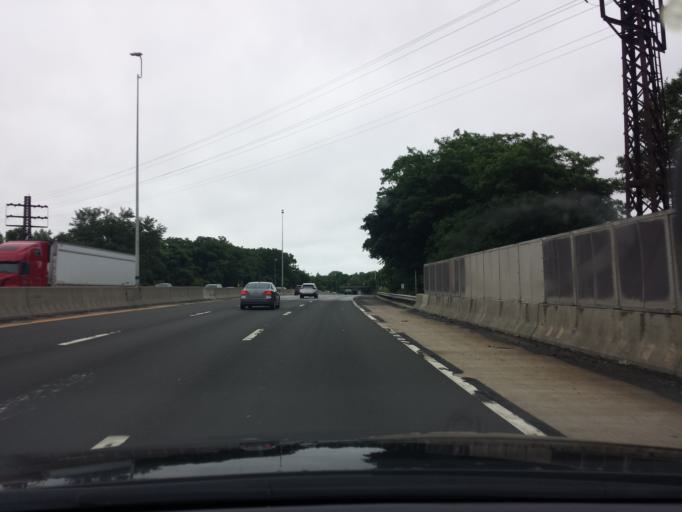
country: US
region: New York
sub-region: Westchester County
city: Rye
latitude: 40.9878
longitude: -73.6764
